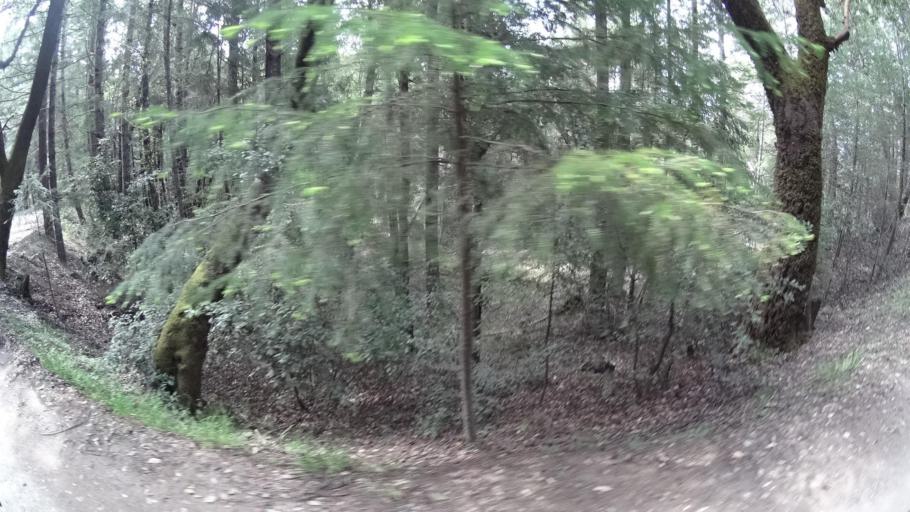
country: US
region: California
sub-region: Humboldt County
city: Redway
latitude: 40.0350
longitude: -123.8392
